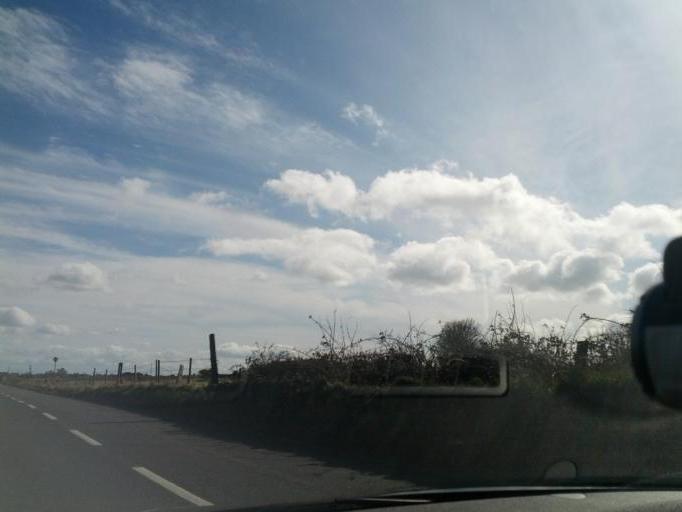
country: IE
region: Leinster
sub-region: Fingal County
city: Baldoyle
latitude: 53.4070
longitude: -6.1351
